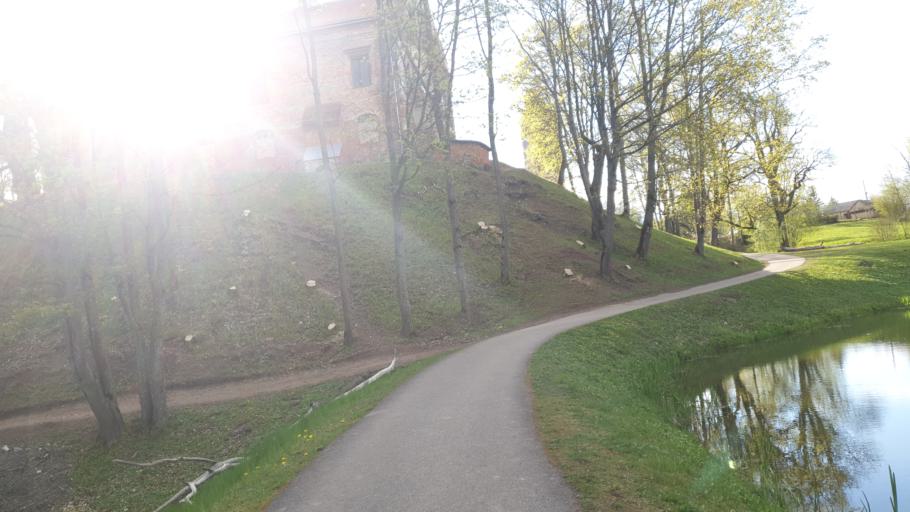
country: LT
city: Gelgaudiskis
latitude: 55.0989
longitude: 22.9882
